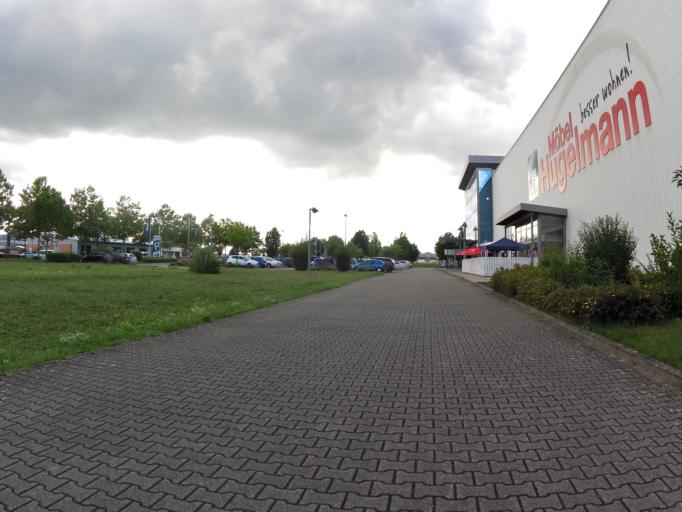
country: DE
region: Baden-Wuerttemberg
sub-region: Freiburg Region
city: Lahr
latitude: 48.3501
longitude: 7.8233
